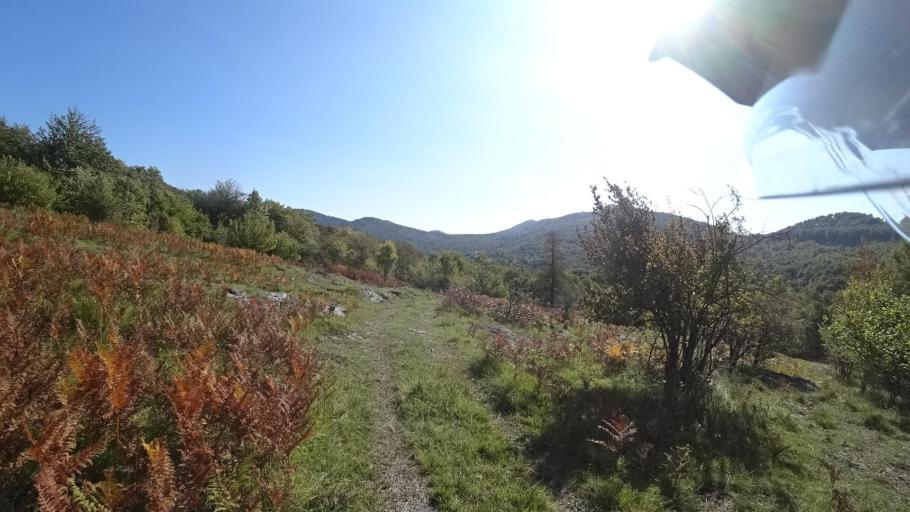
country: HR
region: Karlovacka
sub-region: Grad Ogulin
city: Ogulin
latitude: 45.1901
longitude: 15.1269
